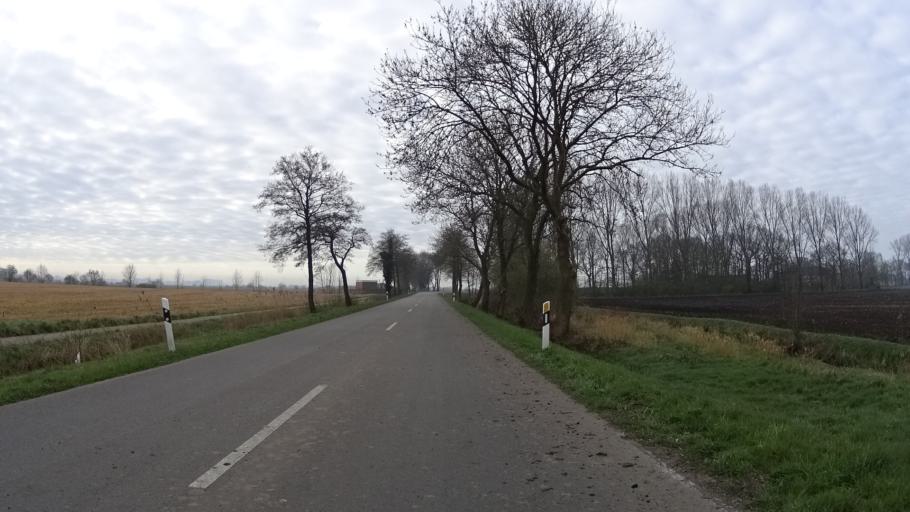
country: DE
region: Lower Saxony
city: Upgant-Schott
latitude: 53.4445
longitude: 7.3306
